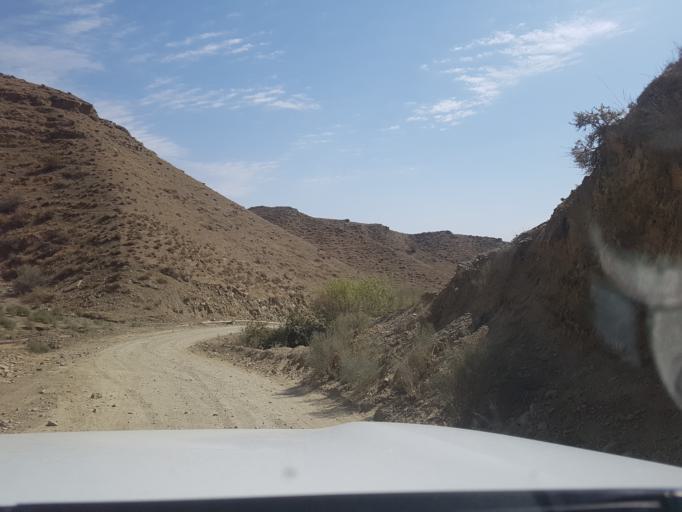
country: TM
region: Ahal
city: Baharly
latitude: 38.2398
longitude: 56.8906
